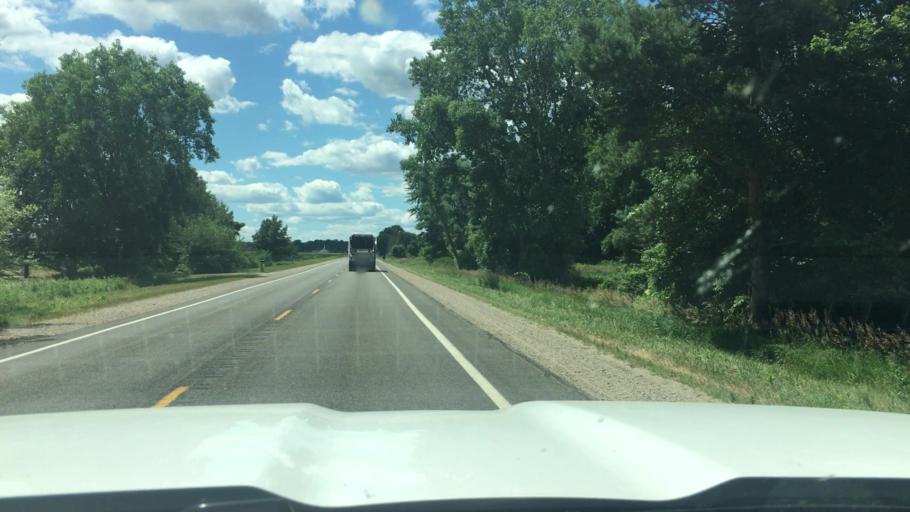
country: US
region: Michigan
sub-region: Montcalm County
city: Carson City
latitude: 43.1775
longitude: -84.9885
